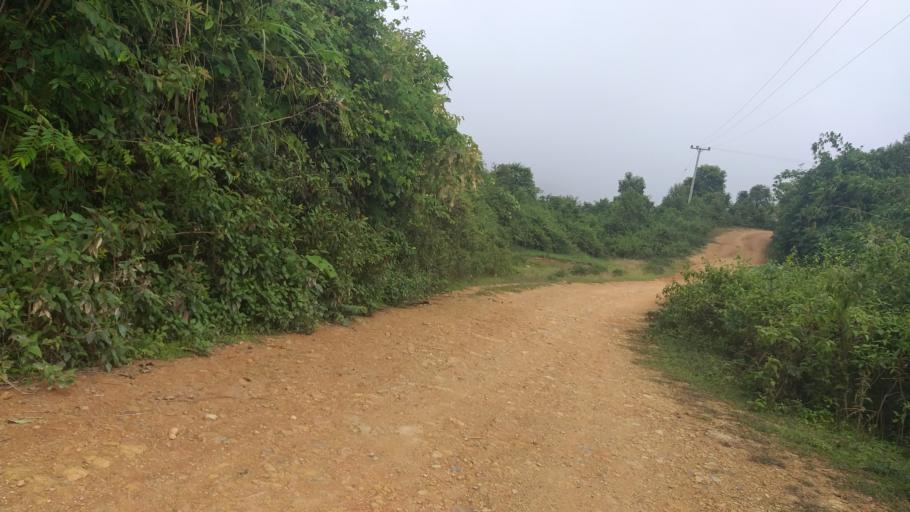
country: LA
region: Phongsali
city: Khoa
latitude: 21.2851
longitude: 102.6421
